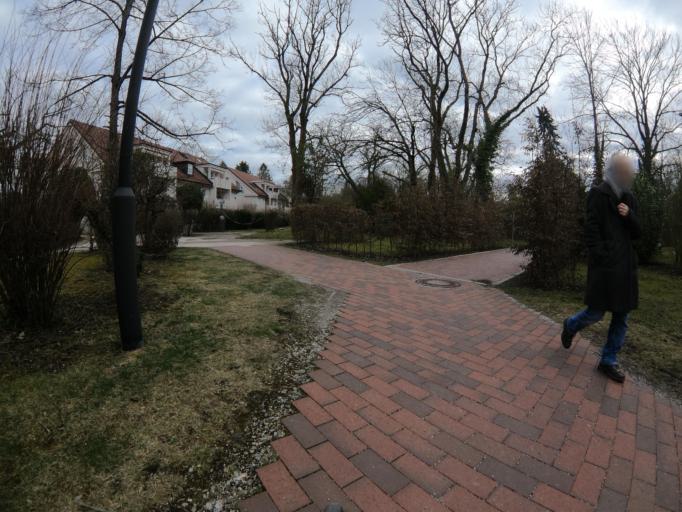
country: DE
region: Bavaria
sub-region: Upper Bavaria
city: Fuerstenfeldbruck
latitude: 48.1824
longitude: 11.2622
